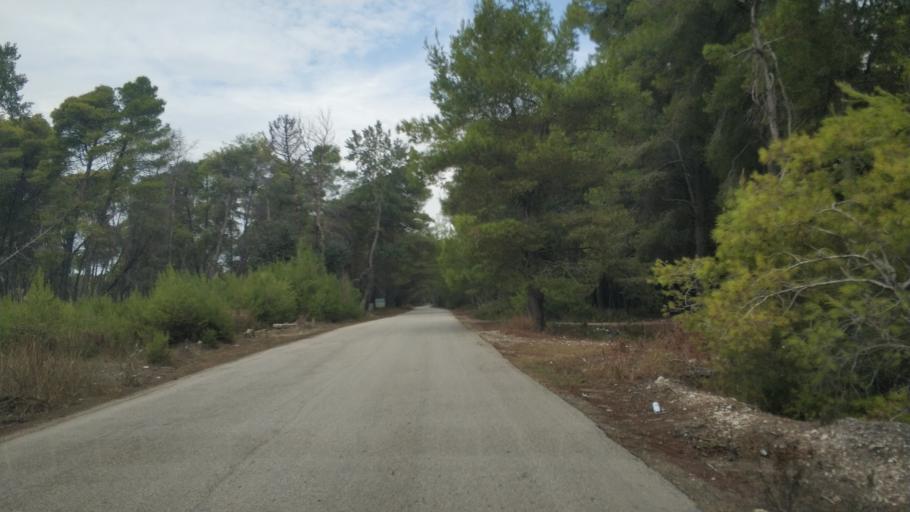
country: AL
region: Vlore
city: Vlore
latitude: 40.4815
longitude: 19.4489
